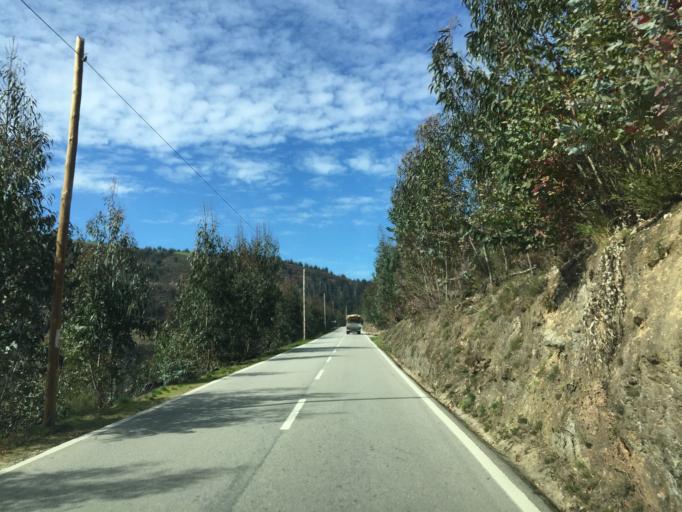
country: PT
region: Aveiro
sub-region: Arouca
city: Arouca
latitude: 40.9625
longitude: -8.2218
